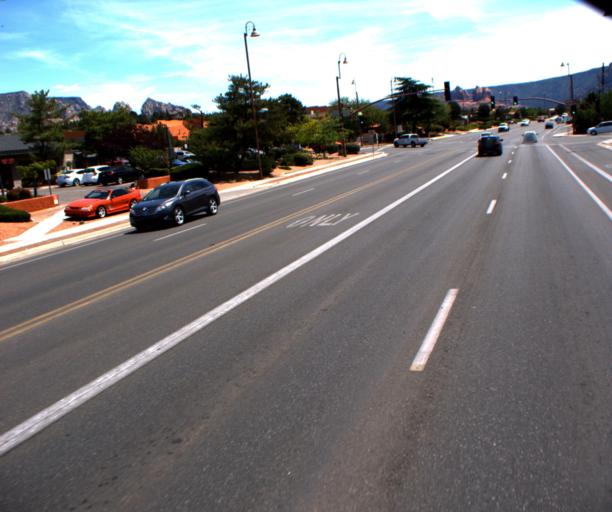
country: US
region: Arizona
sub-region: Yavapai County
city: West Sedona
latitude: 34.8637
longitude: -111.7963
